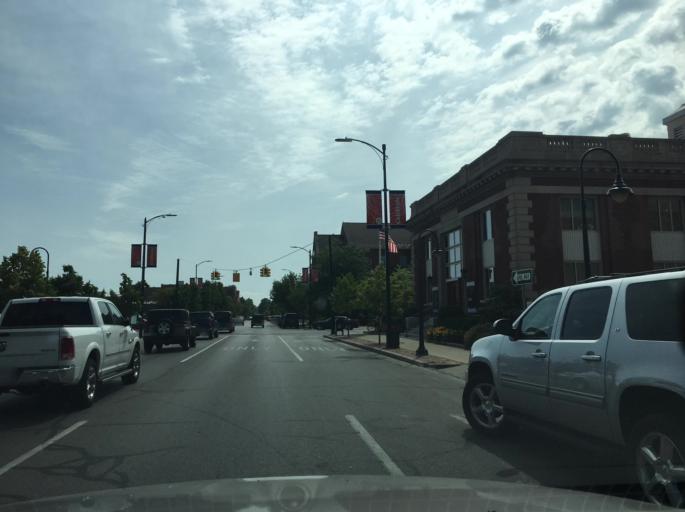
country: US
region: Michigan
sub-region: Grand Traverse County
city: Traverse City
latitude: 44.7629
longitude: -85.6218
